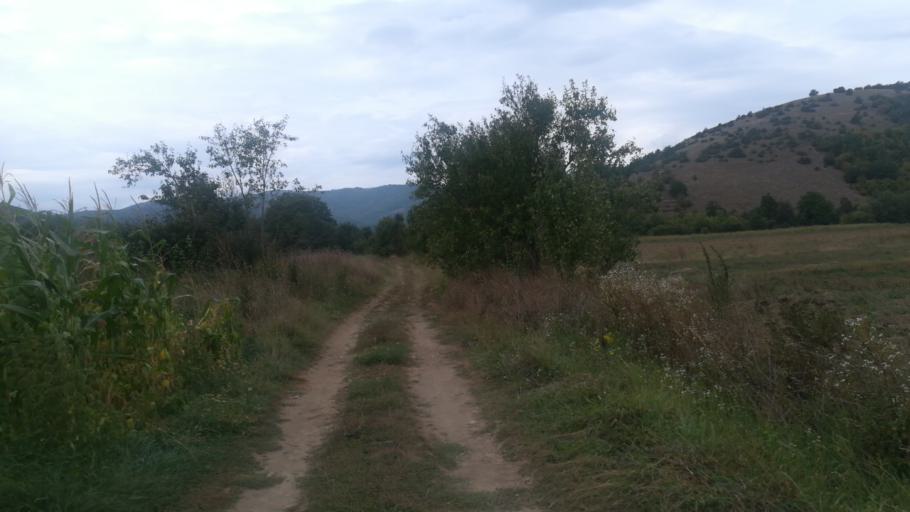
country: MK
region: Debarca
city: Belcista
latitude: 41.2850
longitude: 20.8325
